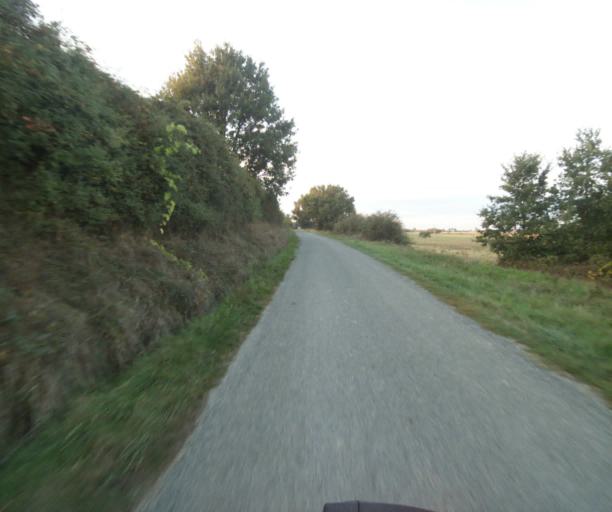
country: FR
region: Midi-Pyrenees
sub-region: Departement du Tarn-et-Garonne
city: Verdun-sur-Garonne
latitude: 43.8252
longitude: 1.2102
